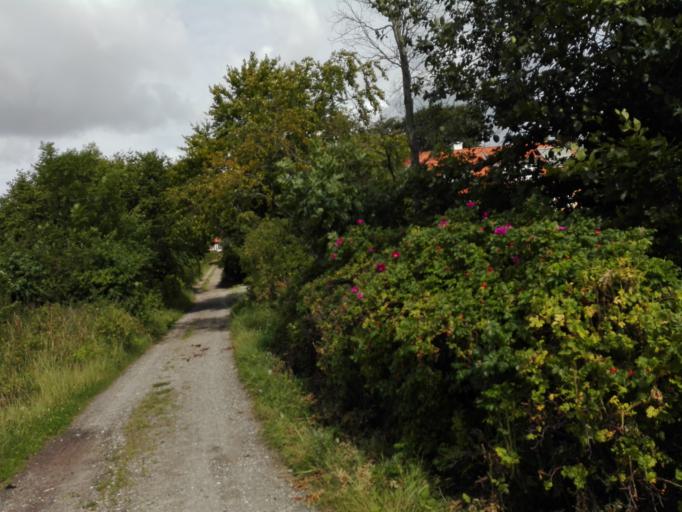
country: DK
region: Central Jutland
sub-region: Arhus Kommune
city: Marslet
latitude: 56.0834
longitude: 10.1820
